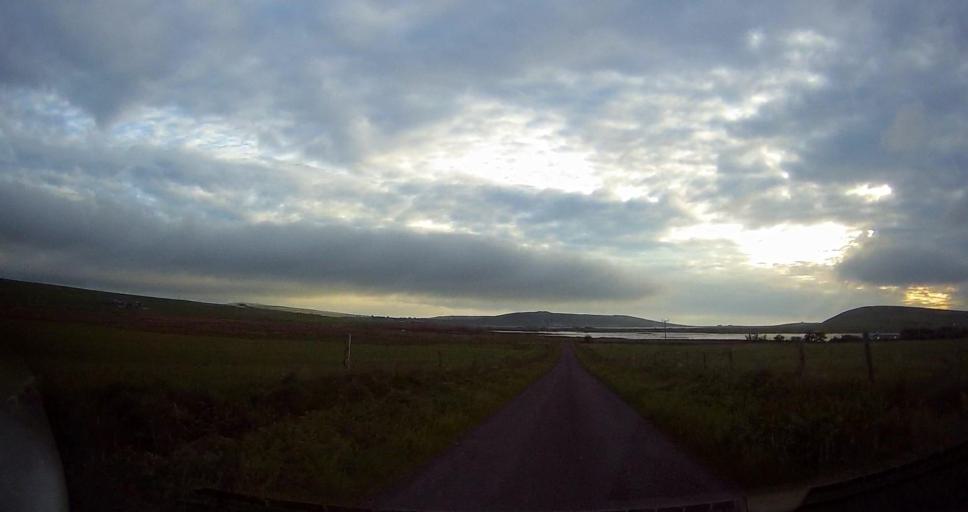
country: GB
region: Scotland
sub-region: Orkney Islands
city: Stromness
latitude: 59.1097
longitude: -3.2239
